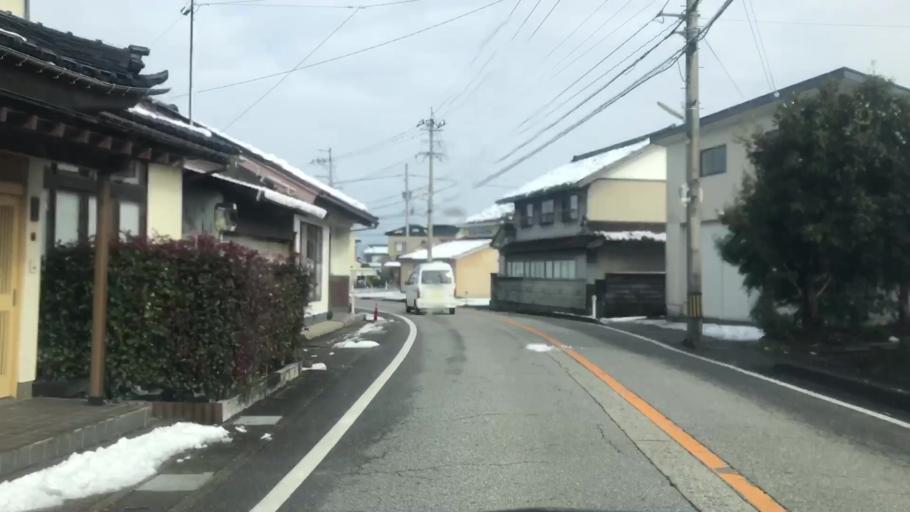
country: JP
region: Toyama
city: Toyama-shi
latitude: 36.6238
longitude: 137.2526
